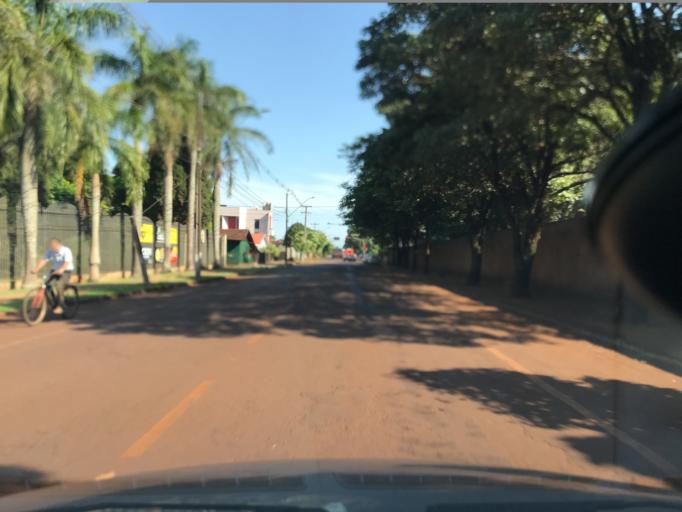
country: BR
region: Parana
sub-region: Palotina
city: Palotina
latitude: -24.2928
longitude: -53.8443
